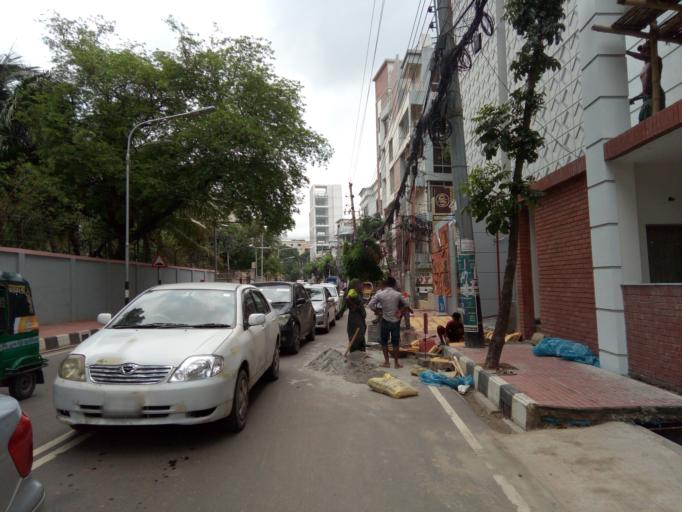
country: BD
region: Dhaka
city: Paltan
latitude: 23.7951
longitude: 90.4084
